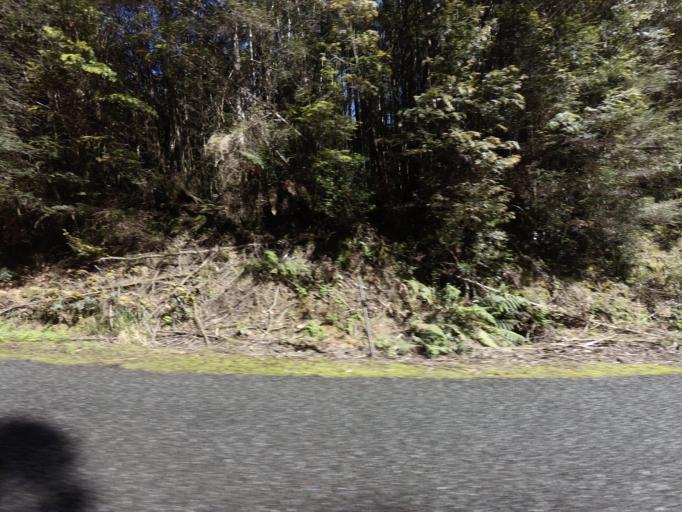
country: AU
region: Tasmania
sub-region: Derwent Valley
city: New Norfolk
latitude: -42.7439
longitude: 146.4161
